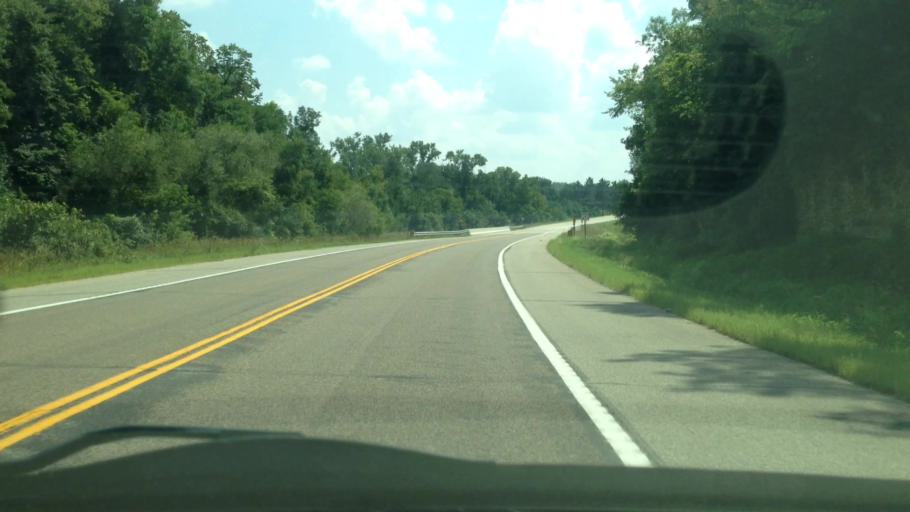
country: US
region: Minnesota
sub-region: Olmsted County
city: Stewartville
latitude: 43.8924
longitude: -92.4084
